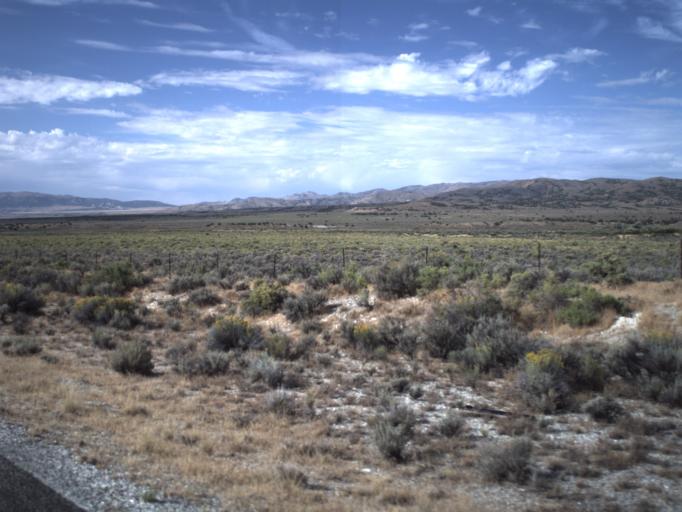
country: US
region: Idaho
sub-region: Cassia County
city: Burley
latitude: 41.6716
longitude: -113.5440
